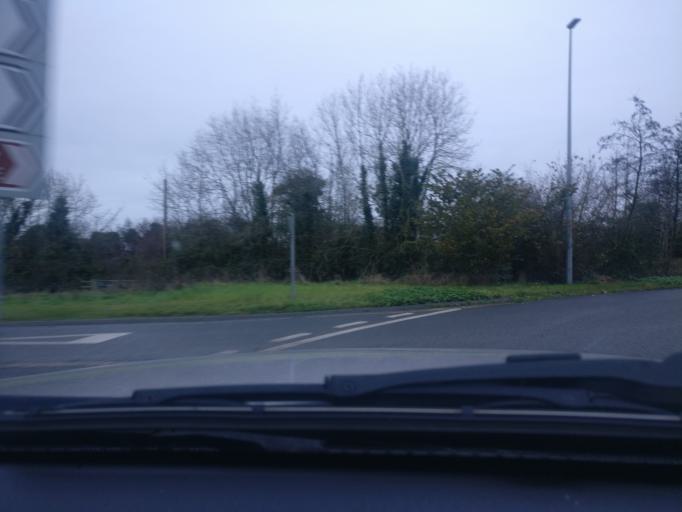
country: IE
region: Leinster
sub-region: An Mhi
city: Dunshaughlin
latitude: 53.5001
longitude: -6.5929
